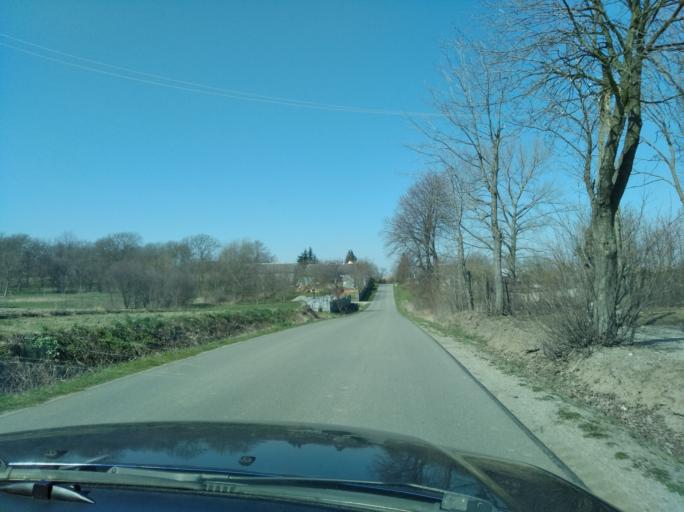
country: PL
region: Subcarpathian Voivodeship
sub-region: Powiat przeworski
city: Pantalowice
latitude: 49.9492
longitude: 22.4383
